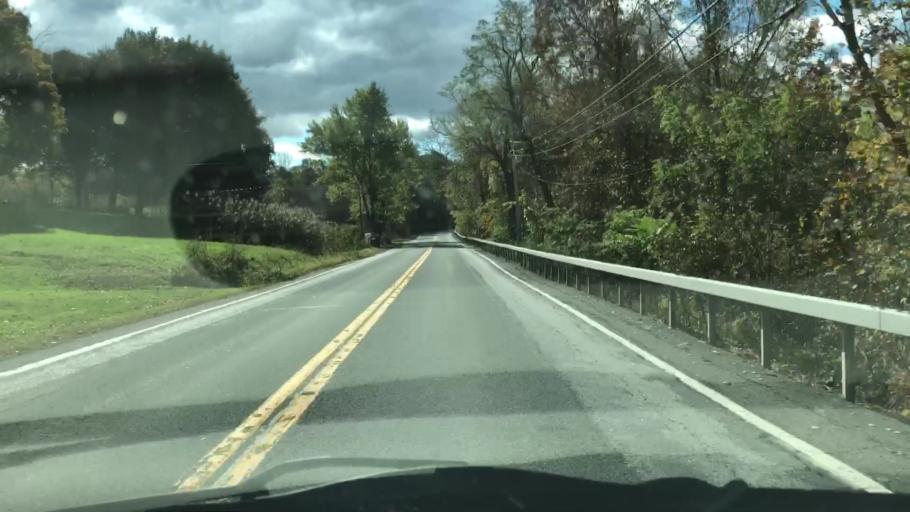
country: US
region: New York
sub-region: Ulster County
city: Wallkill
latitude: 41.5852
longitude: -74.1861
